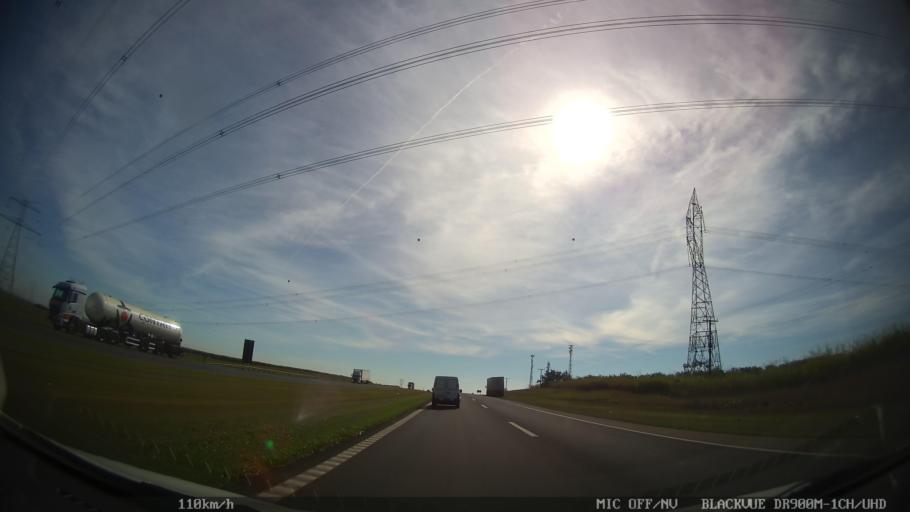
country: BR
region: Sao Paulo
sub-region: Cordeiropolis
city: Cordeiropolis
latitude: -22.4413
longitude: -47.3974
